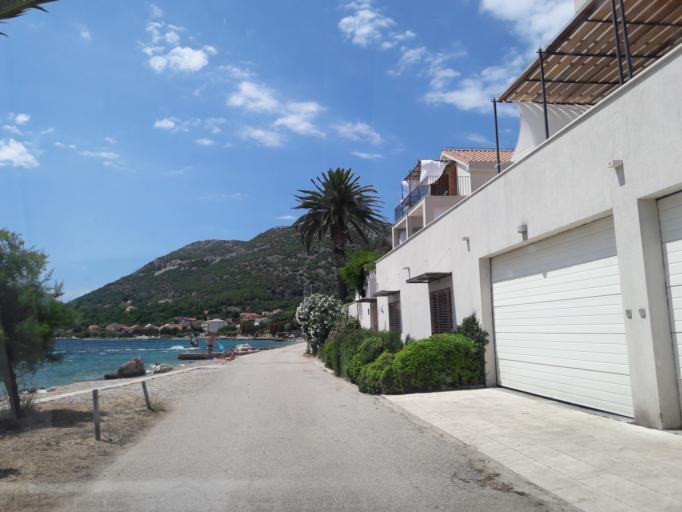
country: HR
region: Dubrovacko-Neretvanska
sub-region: Grad Korcula
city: Zrnovo
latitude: 42.9839
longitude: 17.0982
